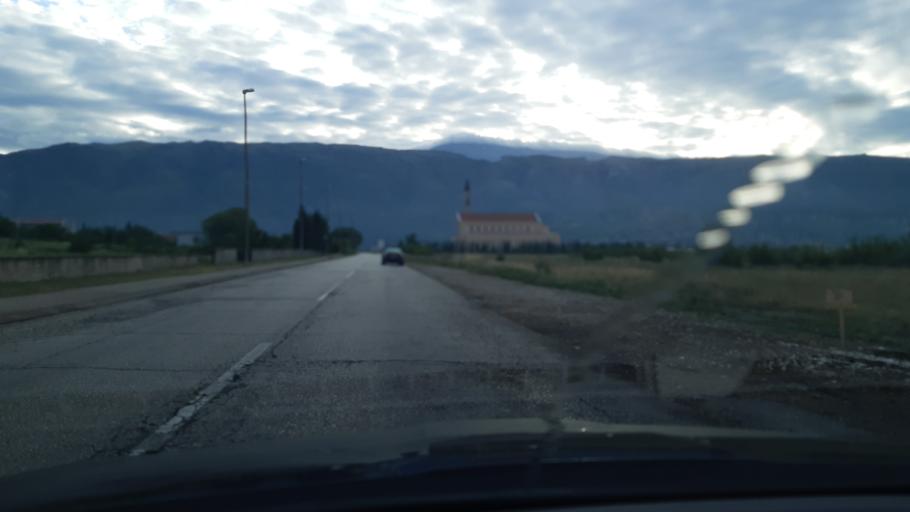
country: BA
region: Federation of Bosnia and Herzegovina
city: Rodoc
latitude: 43.3107
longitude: 17.8104
